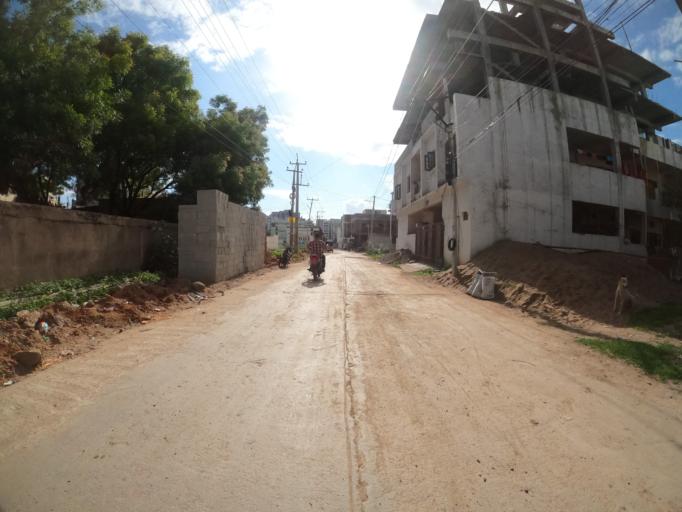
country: IN
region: Telangana
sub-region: Hyderabad
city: Hyderabad
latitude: 17.3600
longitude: 78.3783
